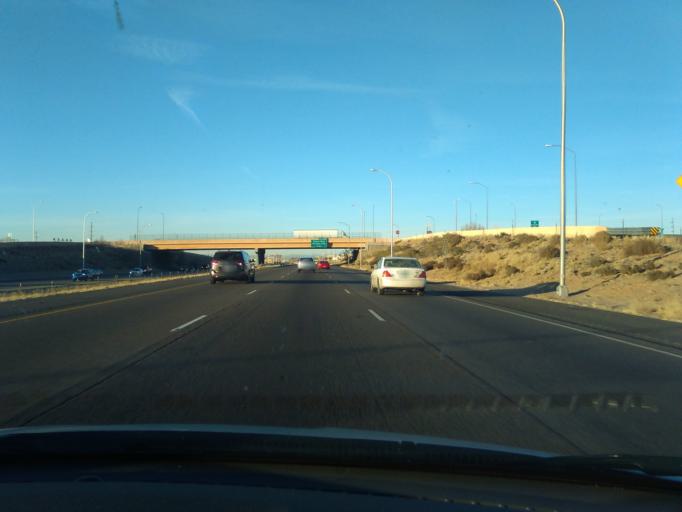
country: US
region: New Mexico
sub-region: Bernalillo County
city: Albuquerque
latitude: 35.0456
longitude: -106.6377
